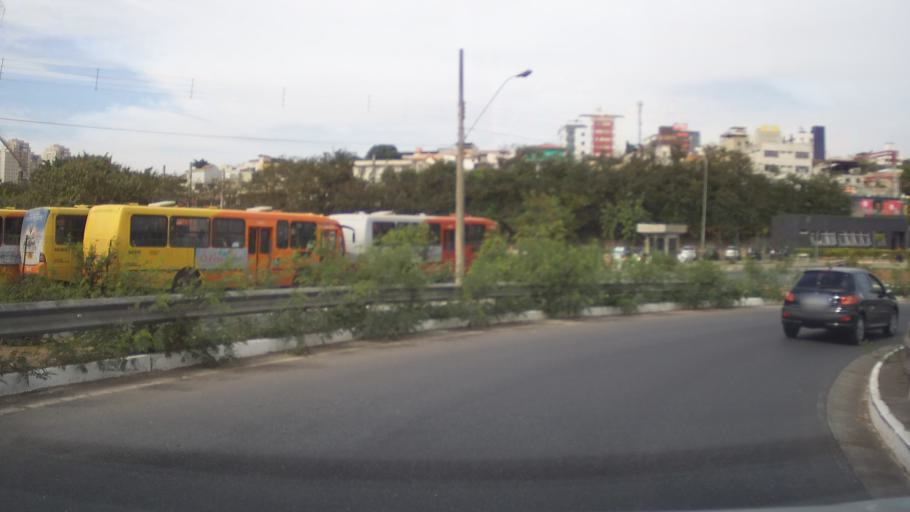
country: BR
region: Minas Gerais
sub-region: Contagem
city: Contagem
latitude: -19.9400
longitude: -44.0287
